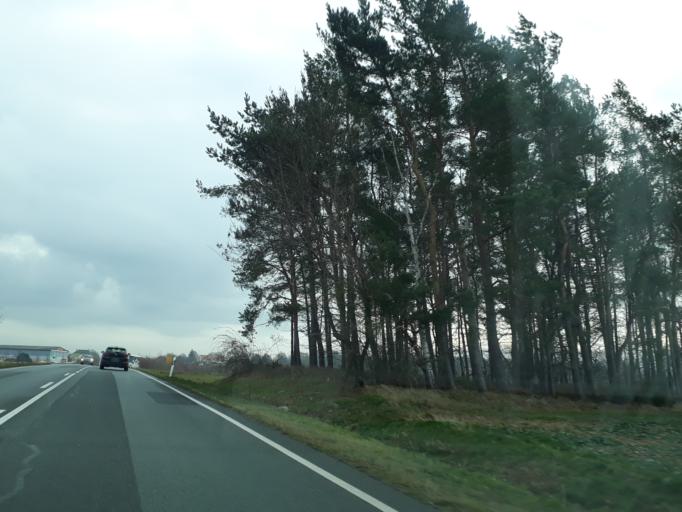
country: DE
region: Saxony
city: Kubschutz
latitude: 51.1659
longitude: 14.4982
